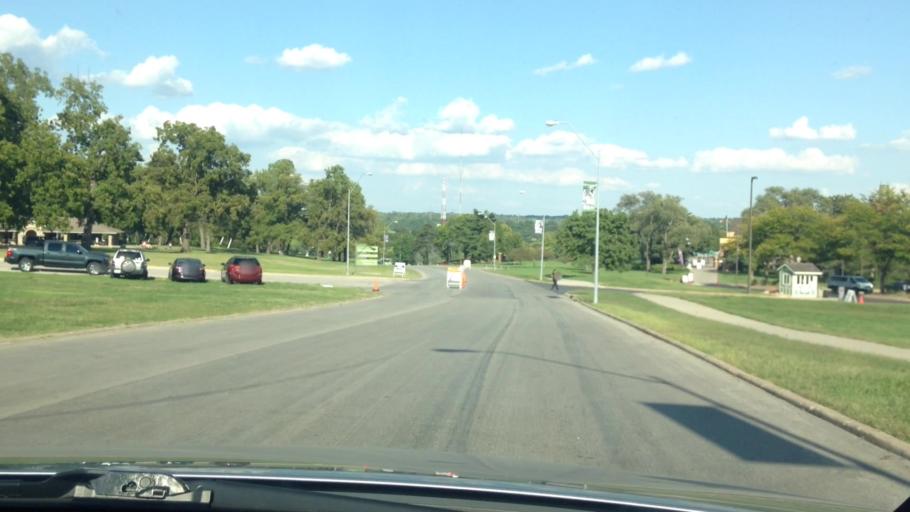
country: US
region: Missouri
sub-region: Jackson County
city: Raytown
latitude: 39.0081
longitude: -94.5358
